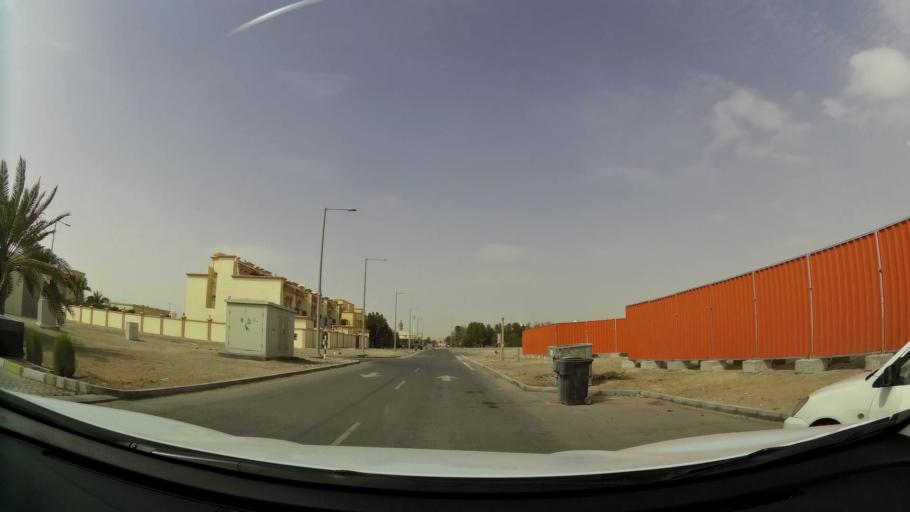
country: AE
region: Abu Dhabi
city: Abu Dhabi
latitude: 24.4107
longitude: 54.5641
